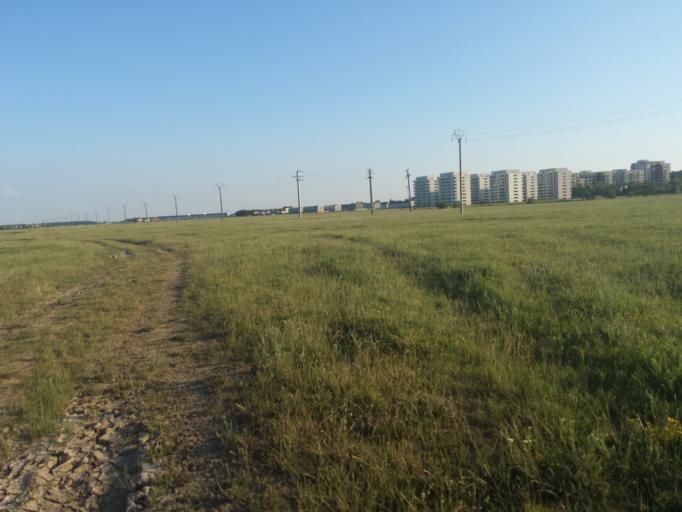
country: RO
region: Ilfov
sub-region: Comuna Tunari
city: Tunari
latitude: 44.5272
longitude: 26.1517
